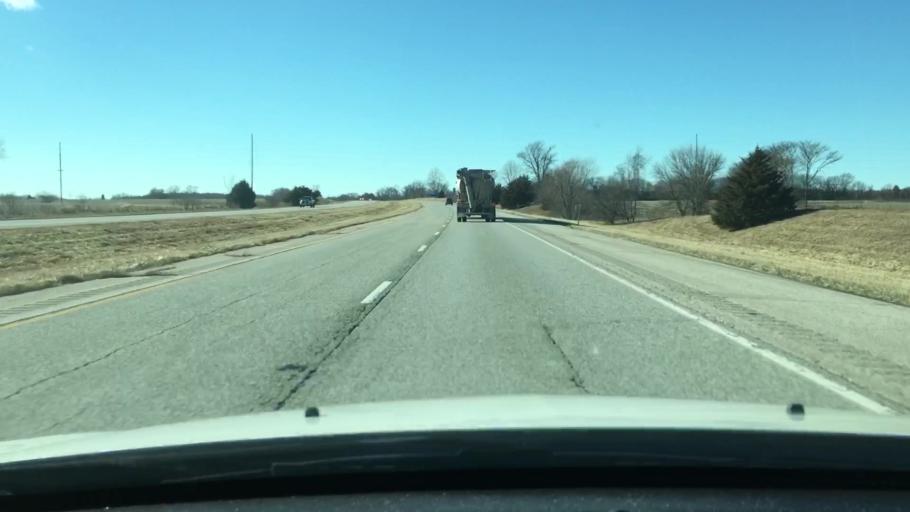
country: US
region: Illinois
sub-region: Pike County
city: Griggsville
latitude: 39.6784
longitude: -90.7205
